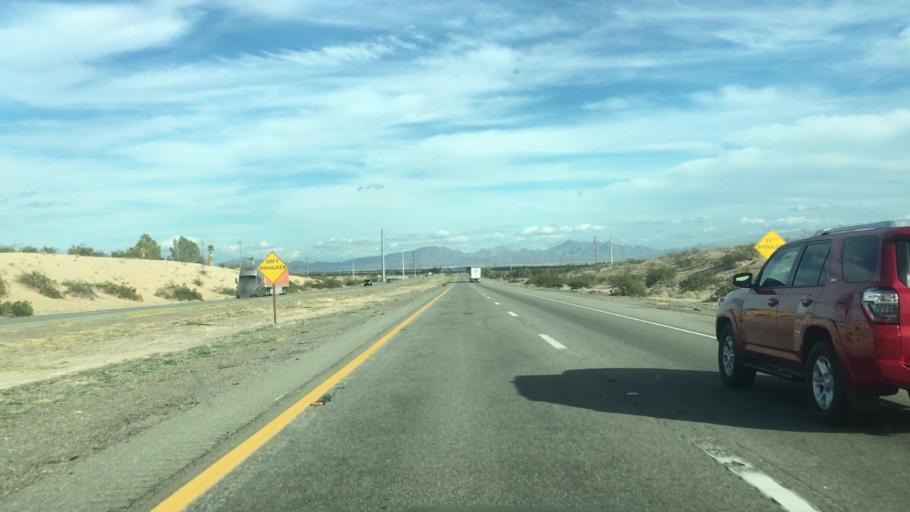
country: US
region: California
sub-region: Riverside County
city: Mesa Verde
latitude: 33.6069
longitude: -114.7040
